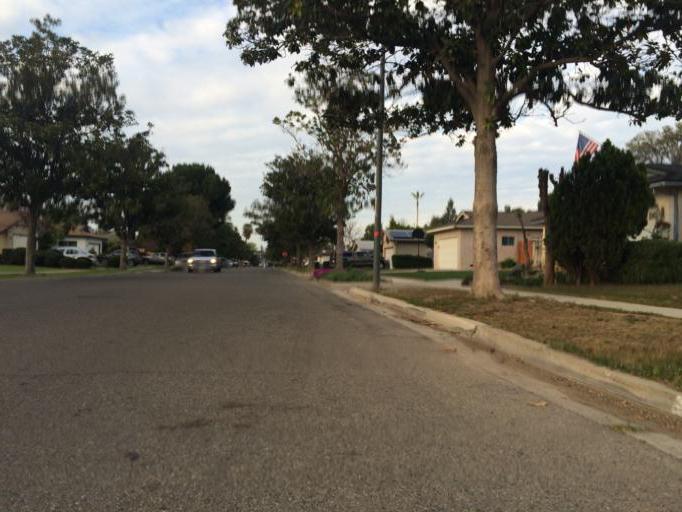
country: US
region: California
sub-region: Fresno County
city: Clovis
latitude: 36.8322
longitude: -119.7614
